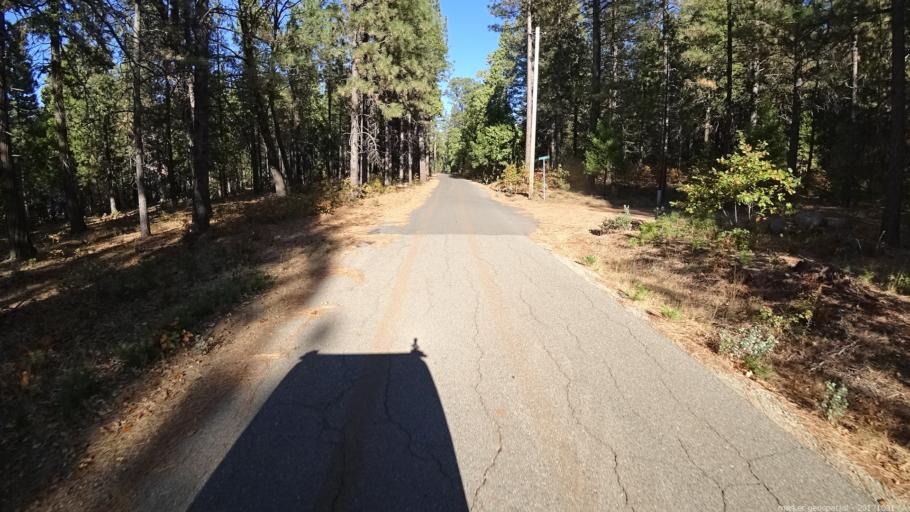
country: US
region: California
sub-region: Shasta County
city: Shingletown
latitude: 40.4904
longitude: -121.9224
